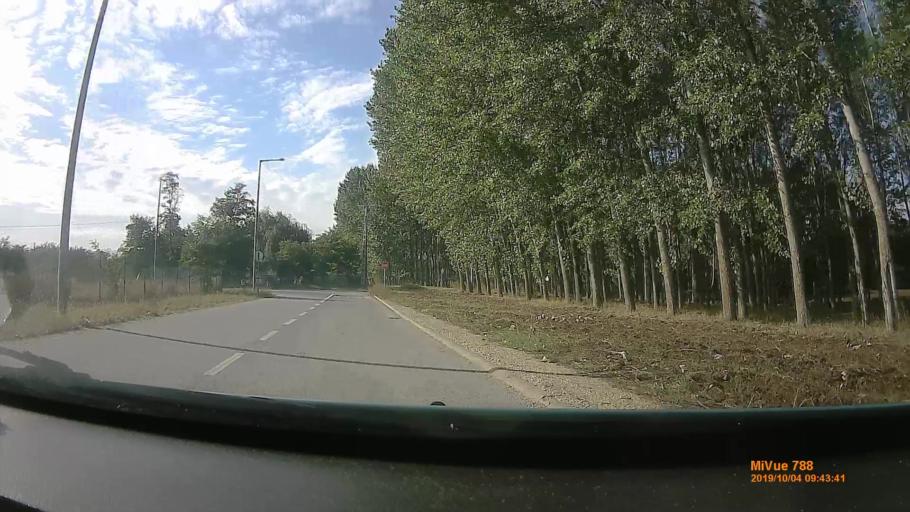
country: HU
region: Szabolcs-Szatmar-Bereg
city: Nyiregyhaza
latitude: 47.9454
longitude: 21.6463
